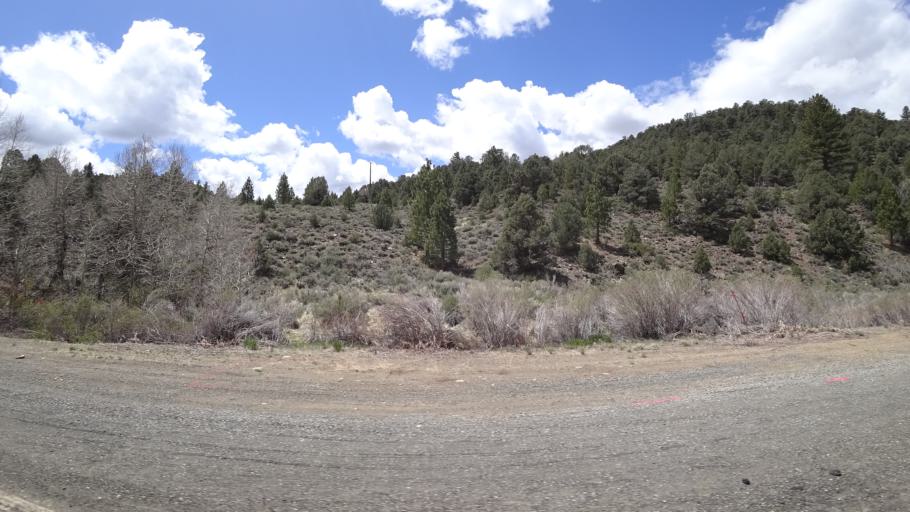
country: US
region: California
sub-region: Mono County
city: Bridgeport
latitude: 38.2833
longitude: -119.3012
